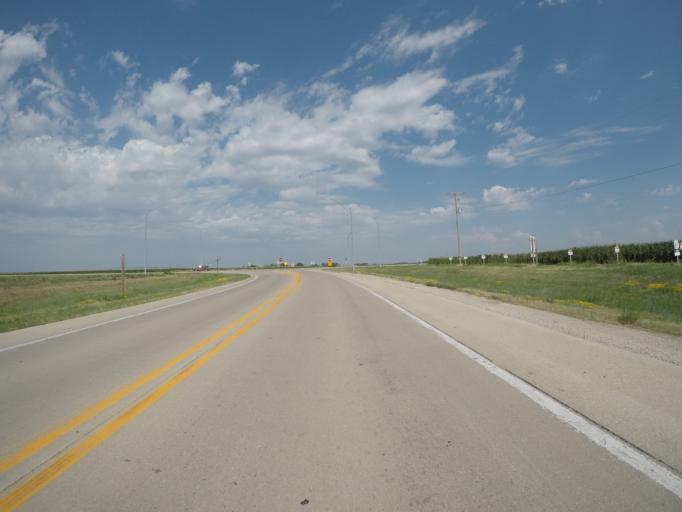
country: US
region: Nebraska
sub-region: Thayer County
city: Hebron
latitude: 40.0166
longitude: -97.6133
